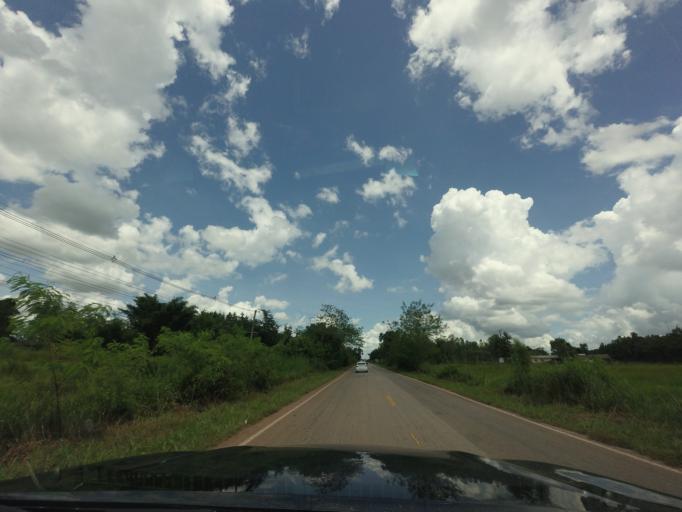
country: TH
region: Changwat Udon Thani
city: Ban Dung
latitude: 17.6815
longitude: 103.1895
